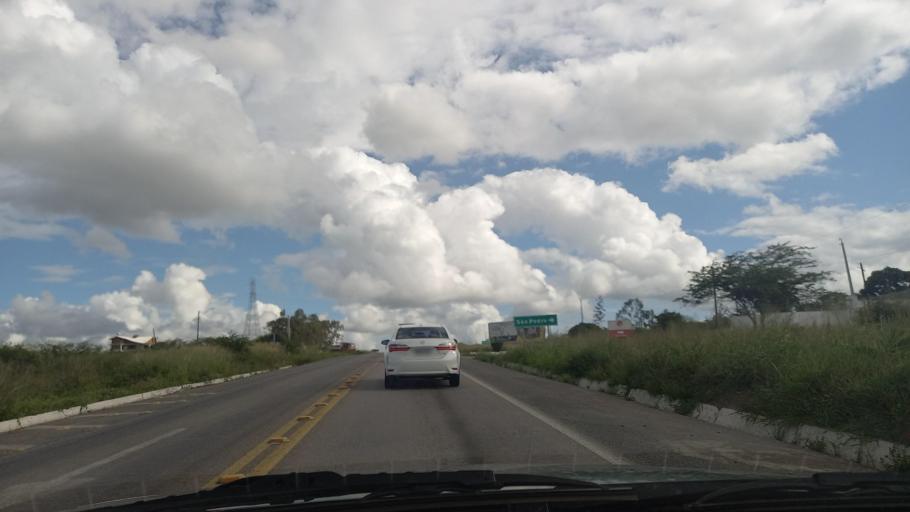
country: BR
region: Pernambuco
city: Garanhuns
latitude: -8.8310
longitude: -36.4529
